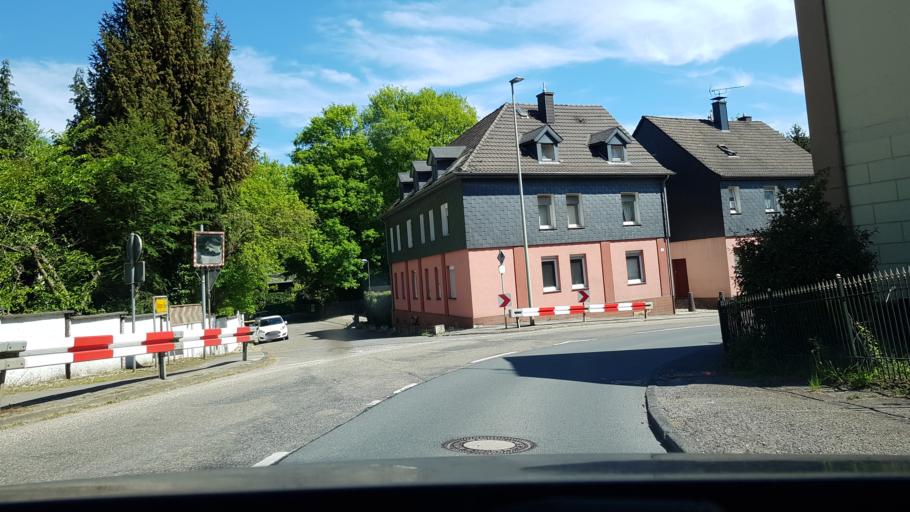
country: DE
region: North Rhine-Westphalia
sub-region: Regierungsbezirk Dusseldorf
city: Heiligenhaus
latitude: 51.3071
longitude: 6.9475
